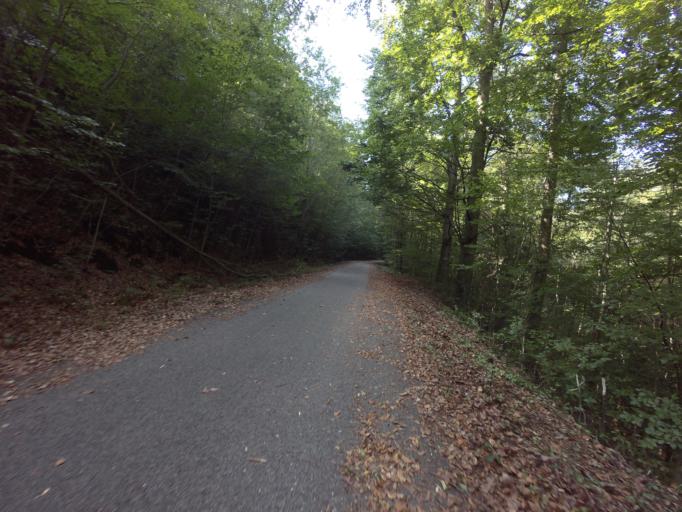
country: CZ
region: Jihocesky
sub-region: Okres Ceske Budejovice
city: Hluboka nad Vltavou
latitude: 49.0897
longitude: 14.4634
